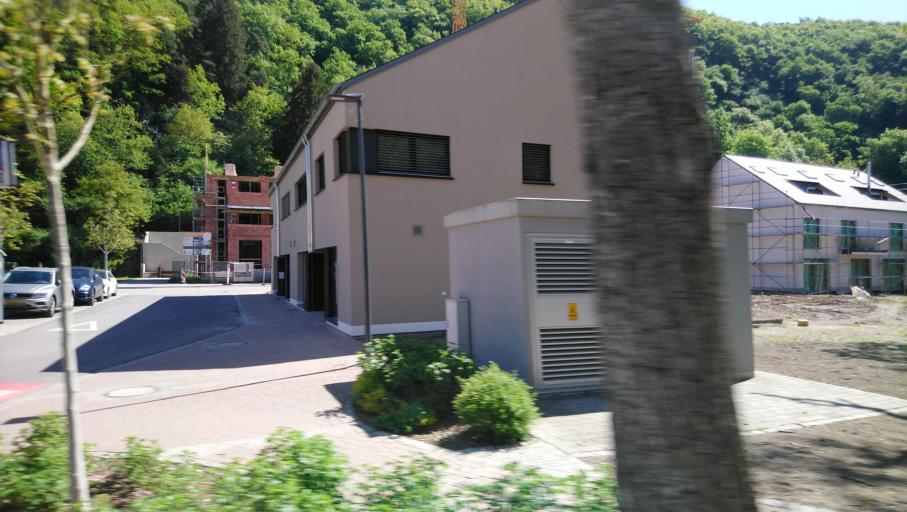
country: LU
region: Diekirch
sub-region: Canton de Vianden
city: Vianden
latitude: 49.9308
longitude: 6.2218
